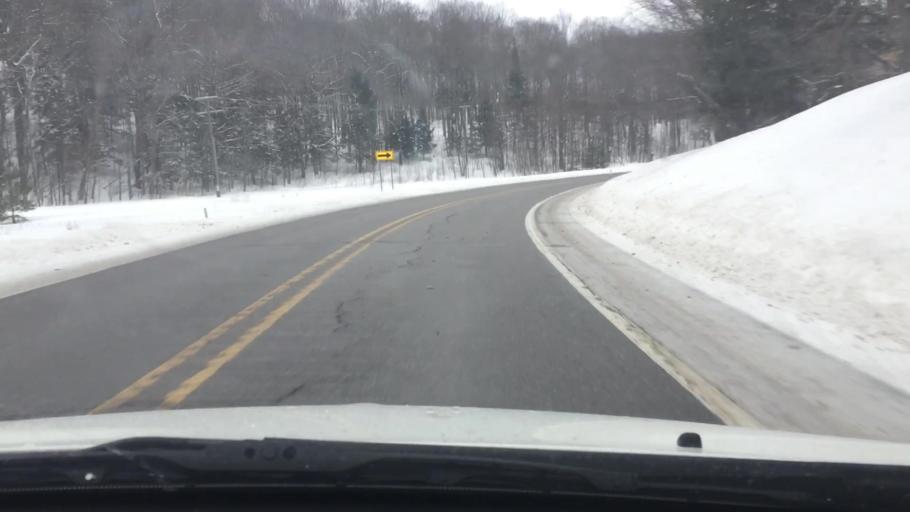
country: US
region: Michigan
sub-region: Charlevoix County
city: Boyne City
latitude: 45.0842
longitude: -84.9351
